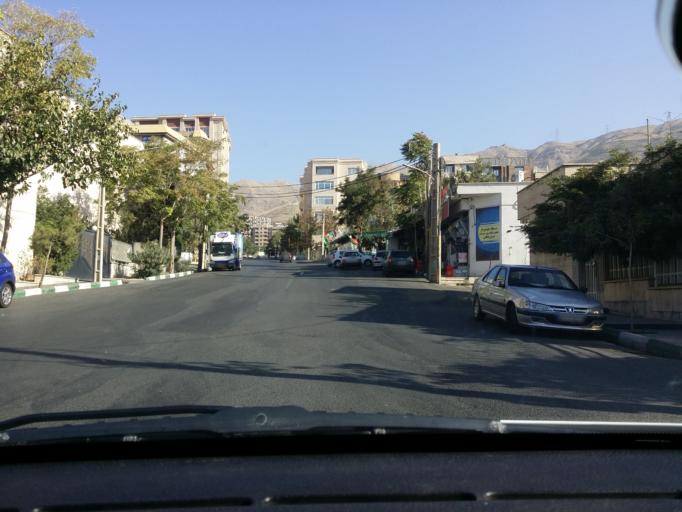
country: IR
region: Alborz
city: Karaj
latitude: 35.8311
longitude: 51.0222
